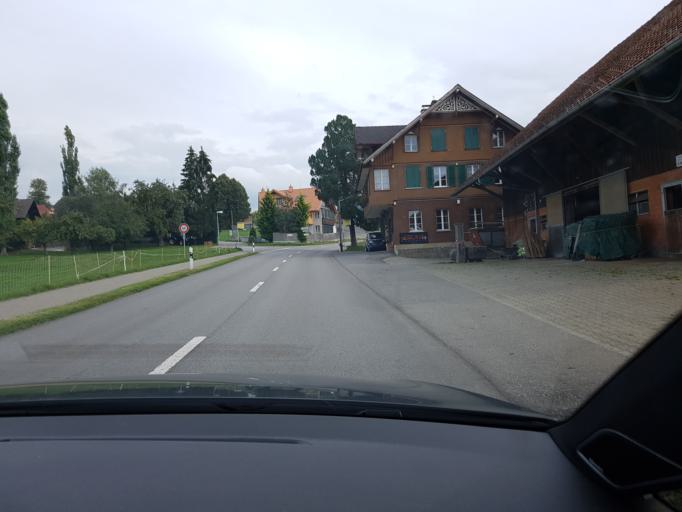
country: CH
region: Bern
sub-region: Thun District
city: Buchholterberg
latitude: 46.7955
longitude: 7.7098
